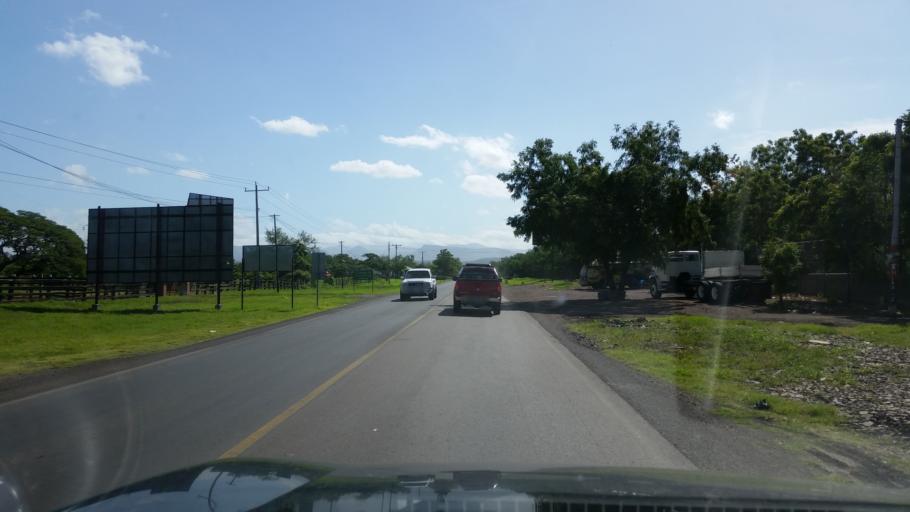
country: NI
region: Matagalpa
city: Ciudad Dario
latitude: 12.8350
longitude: -86.1106
